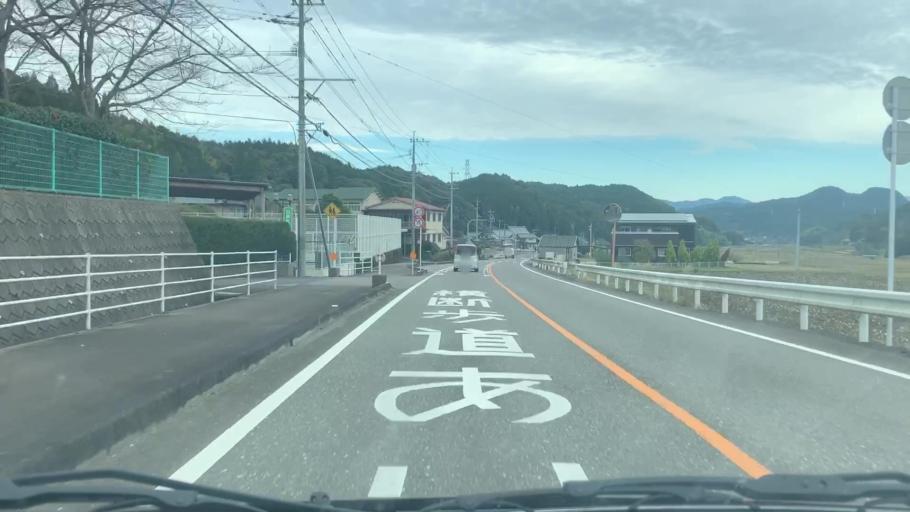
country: JP
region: Saga Prefecture
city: Takeocho-takeo
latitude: 33.1736
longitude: 129.9699
